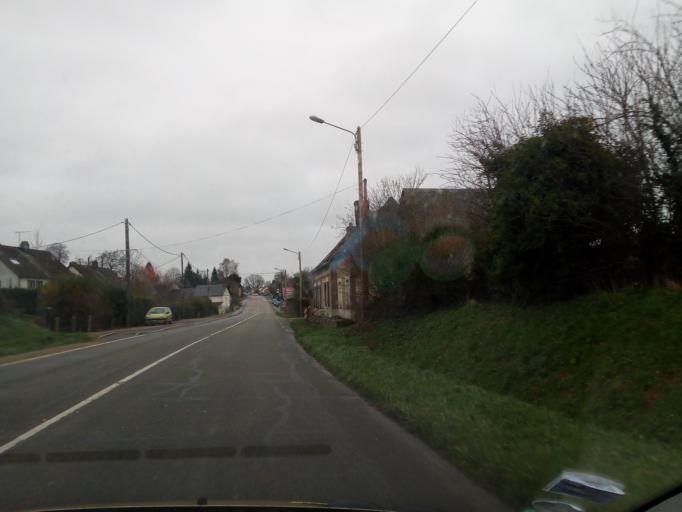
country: FR
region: Haute-Normandie
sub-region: Departement de la Seine-Maritime
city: Yvetot
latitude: 49.6096
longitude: 0.7434
